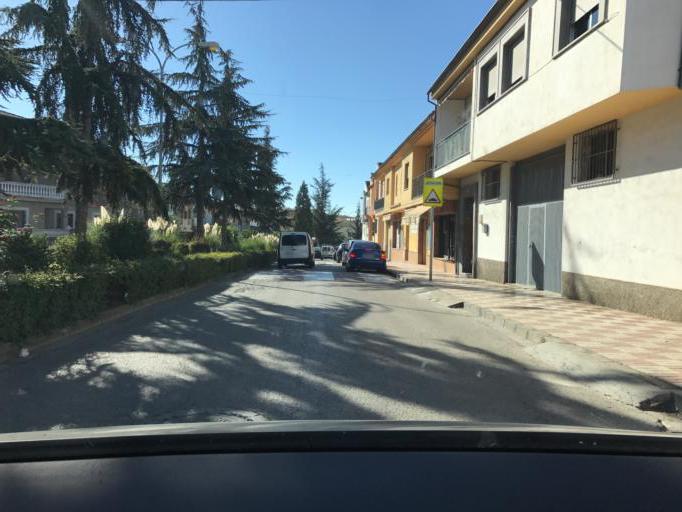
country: ES
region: Andalusia
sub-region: Provincia de Granada
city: Albolote
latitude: 37.2331
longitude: -3.6528
